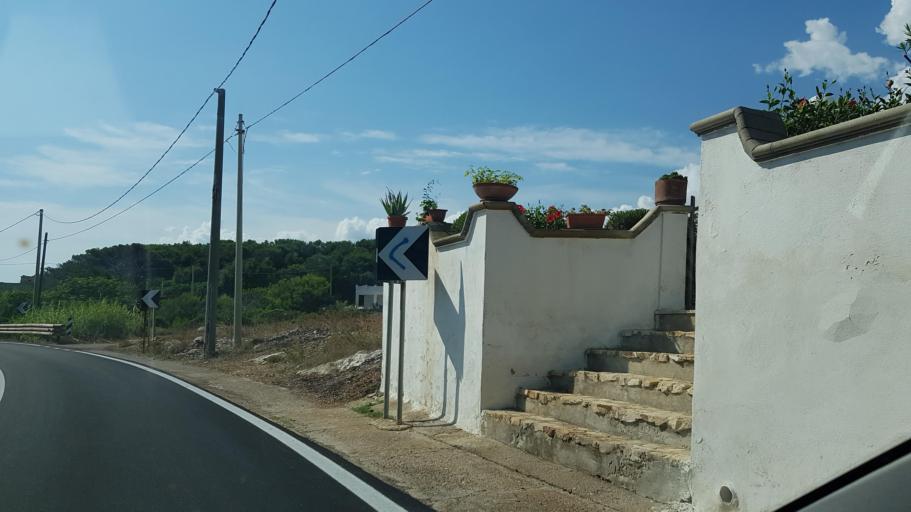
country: IT
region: Apulia
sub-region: Provincia di Lecce
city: Leuca
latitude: 39.7960
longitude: 18.3409
